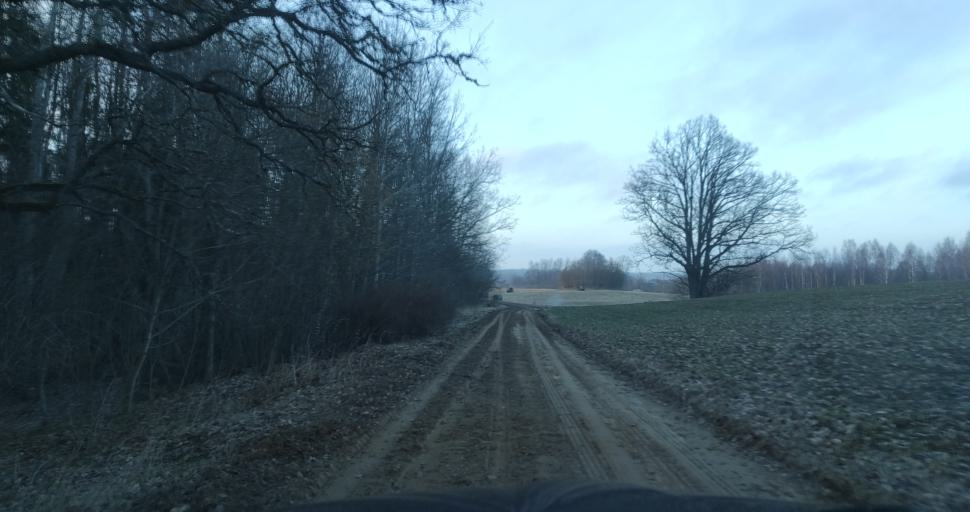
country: LV
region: Aizpute
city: Aizpute
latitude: 56.8057
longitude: 21.8049
